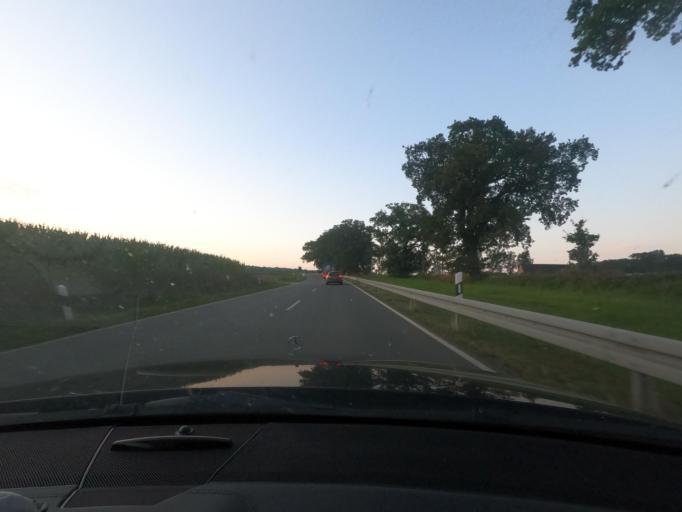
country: DE
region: North Rhine-Westphalia
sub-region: Regierungsbezirk Detmold
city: Salzkotten
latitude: 51.6308
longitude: 8.5851
